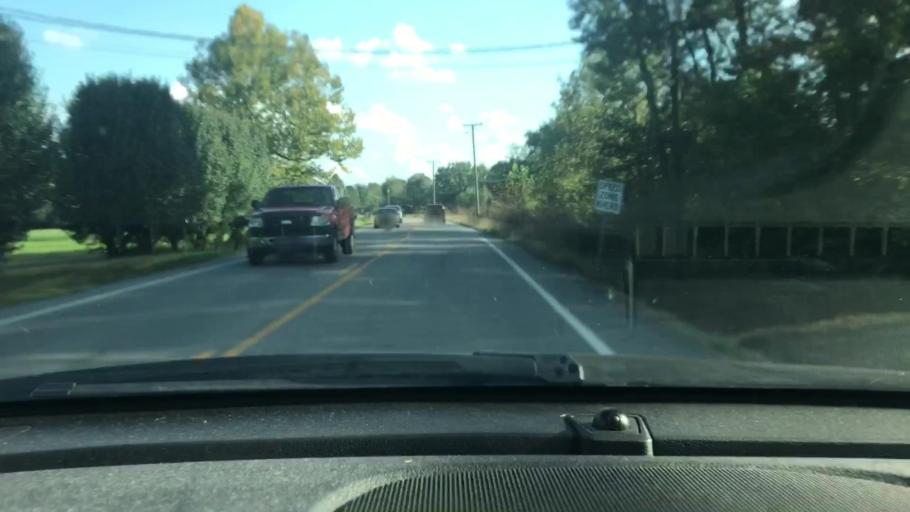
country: US
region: Tennessee
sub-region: Sumner County
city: Shackle Island
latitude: 36.3816
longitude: -86.6203
